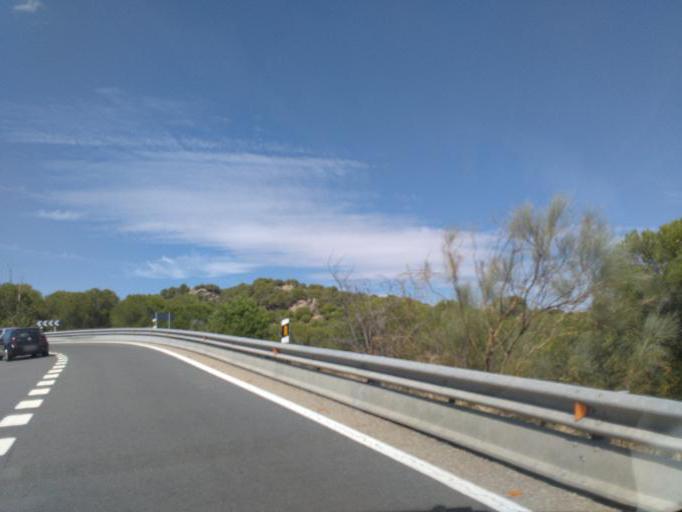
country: ES
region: Madrid
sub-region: Provincia de Madrid
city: Torrelodones
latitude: 40.5524
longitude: -3.9579
